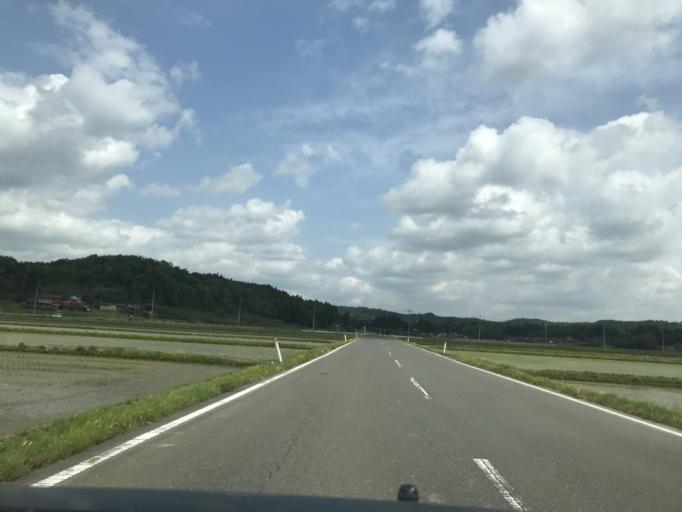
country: JP
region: Iwate
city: Ichinoseki
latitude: 38.8375
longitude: 141.0189
